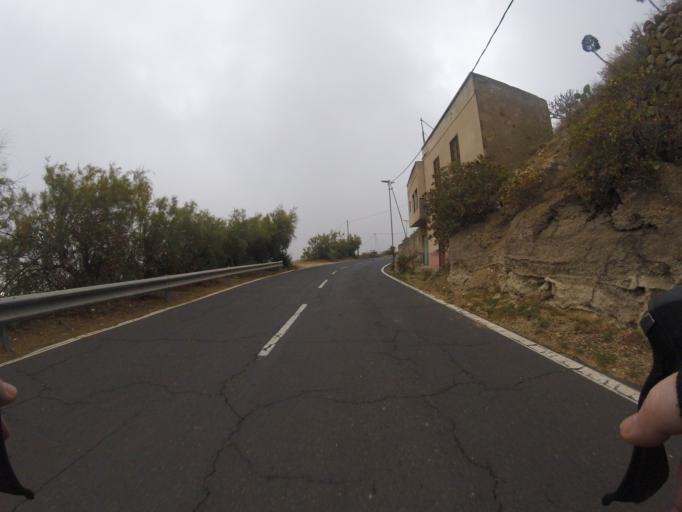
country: ES
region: Canary Islands
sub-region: Provincia de Santa Cruz de Tenerife
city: Guimar
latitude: 28.2824
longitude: -16.4072
